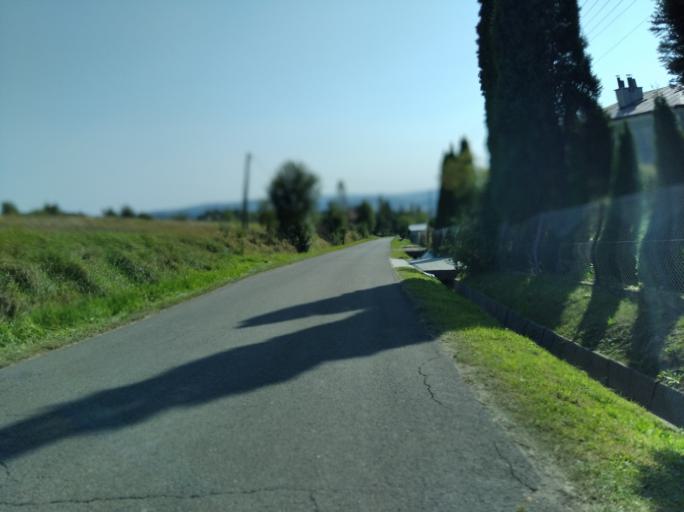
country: PL
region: Subcarpathian Voivodeship
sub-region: Powiat strzyzowski
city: Czudec
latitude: 49.9599
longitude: 21.8283
